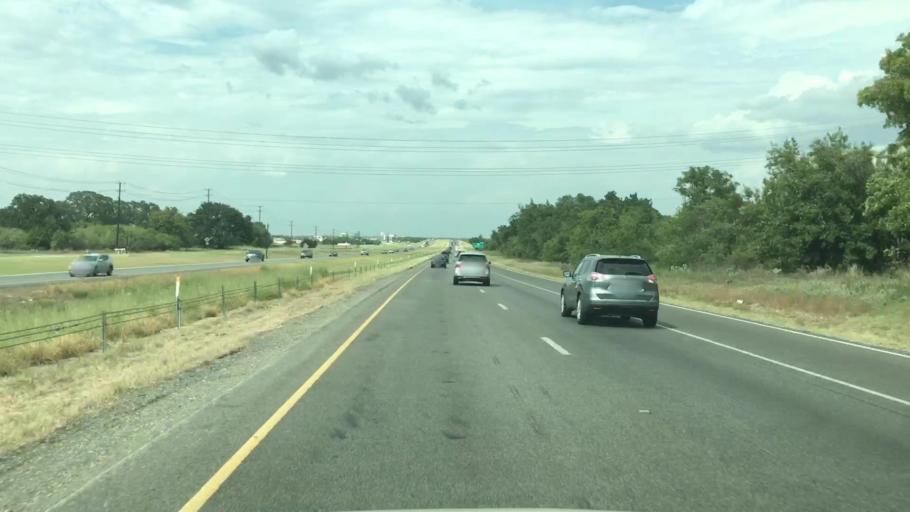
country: US
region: Texas
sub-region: Bexar County
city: Elmendorf
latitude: 29.2059
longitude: -98.4173
